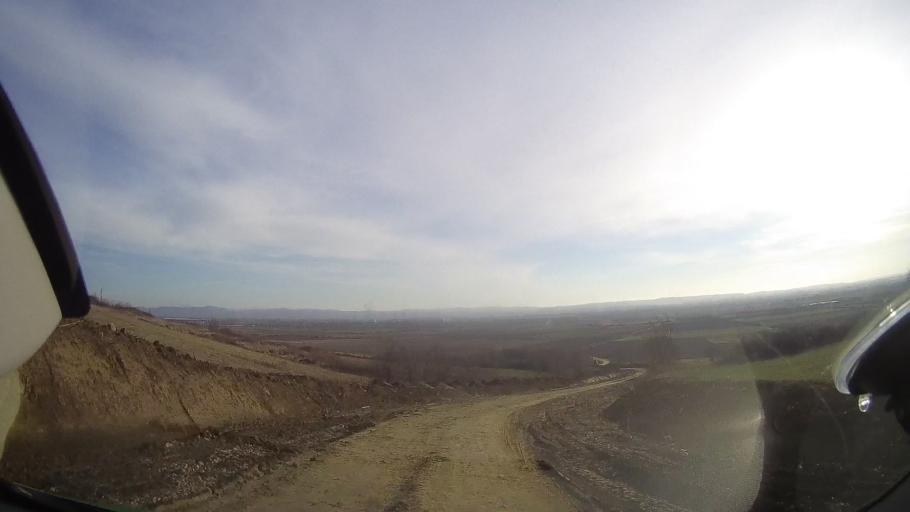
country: RO
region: Bihor
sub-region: Comuna Tileagd
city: Tileagd
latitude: 47.0970
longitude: 22.1775
